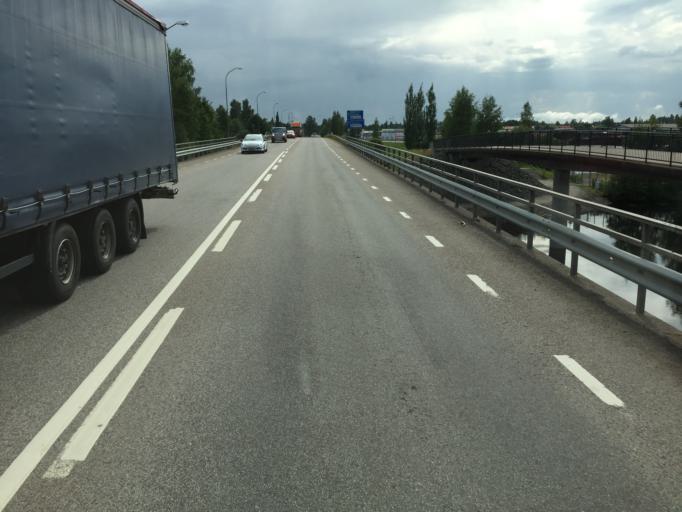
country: SE
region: Dalarna
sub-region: Vansbro Kommun
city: Vansbro
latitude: 60.5121
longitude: 14.2389
